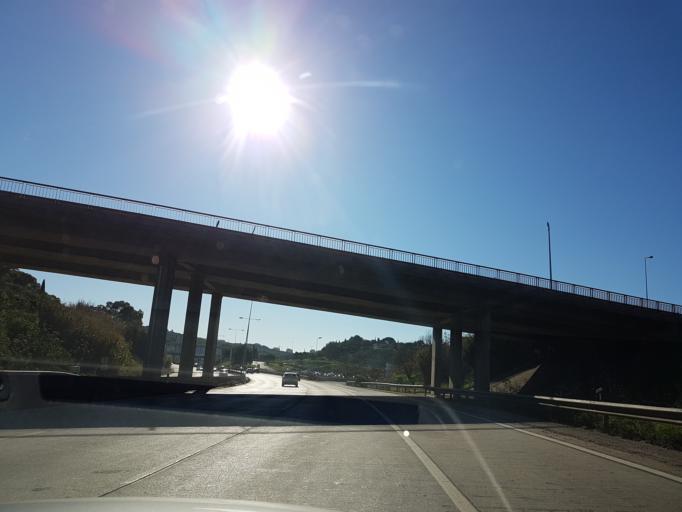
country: PT
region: Lisbon
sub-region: Amadora
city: Amadora
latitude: 38.7297
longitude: -9.2103
